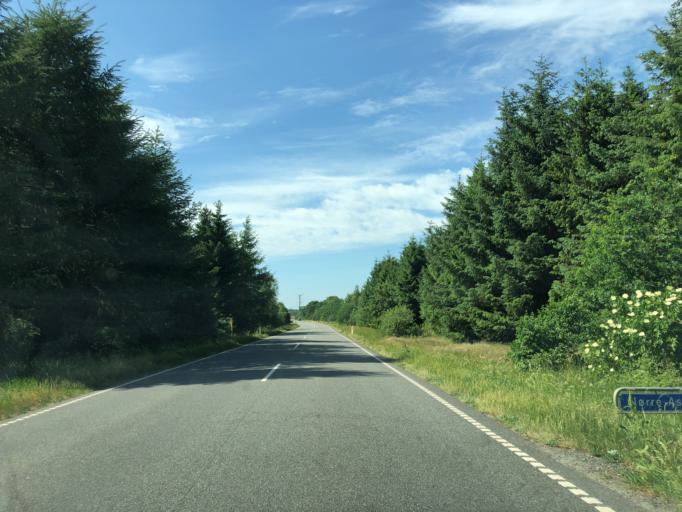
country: DK
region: Central Jutland
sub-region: Ikast-Brande Kommune
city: Brande
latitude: 55.9112
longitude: 9.1836
